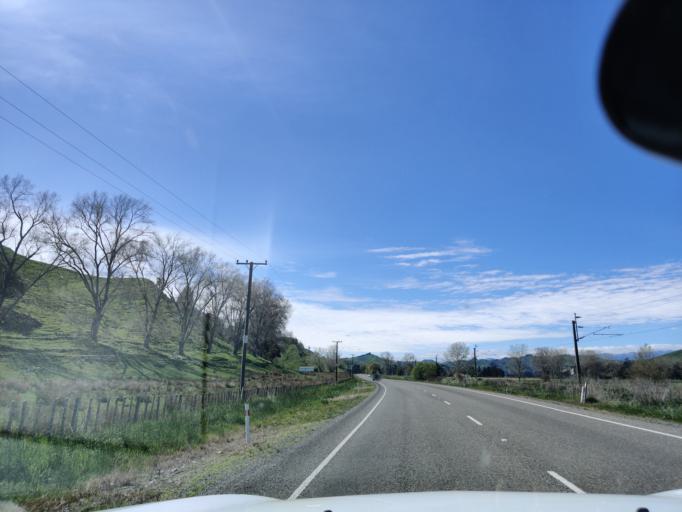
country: NZ
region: Manawatu-Wanganui
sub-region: Ruapehu District
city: Waiouru
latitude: -39.8547
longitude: 175.7262
